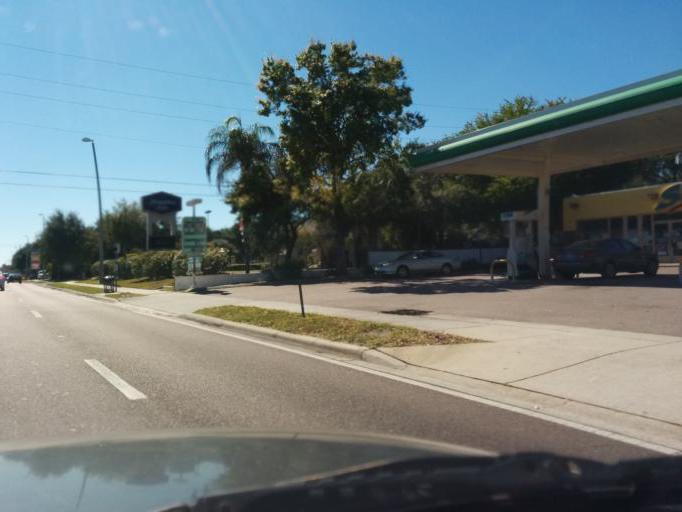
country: US
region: Florida
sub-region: Pinellas County
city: Saint Petersburg
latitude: 27.7844
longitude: -82.6795
